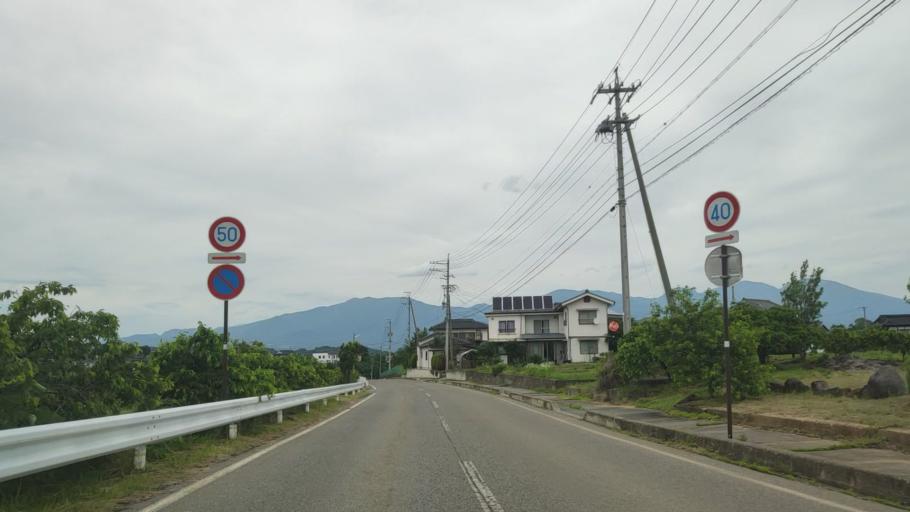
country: JP
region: Nagano
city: Kamimaruko
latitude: 36.2950
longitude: 138.3177
